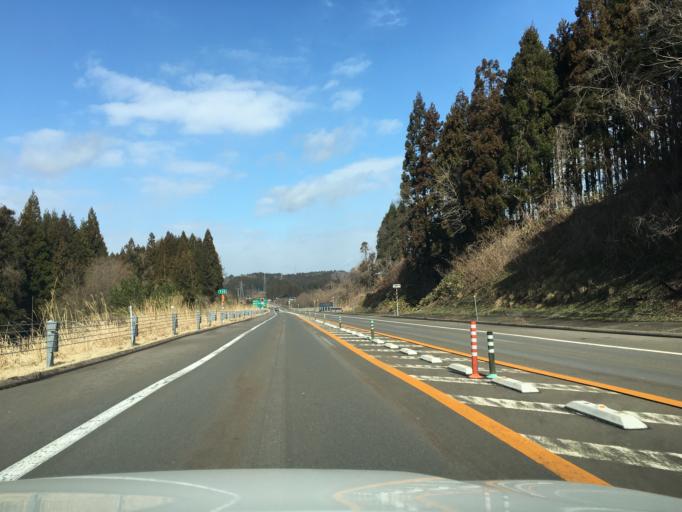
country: JP
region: Akita
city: Akita
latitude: 39.7326
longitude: 140.1771
